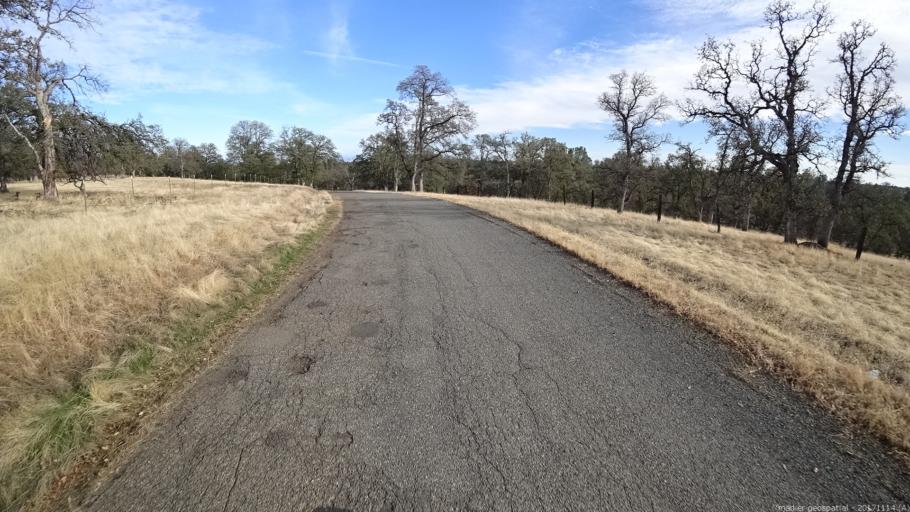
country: US
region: California
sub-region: Shasta County
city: Shasta
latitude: 40.3811
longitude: -122.5691
